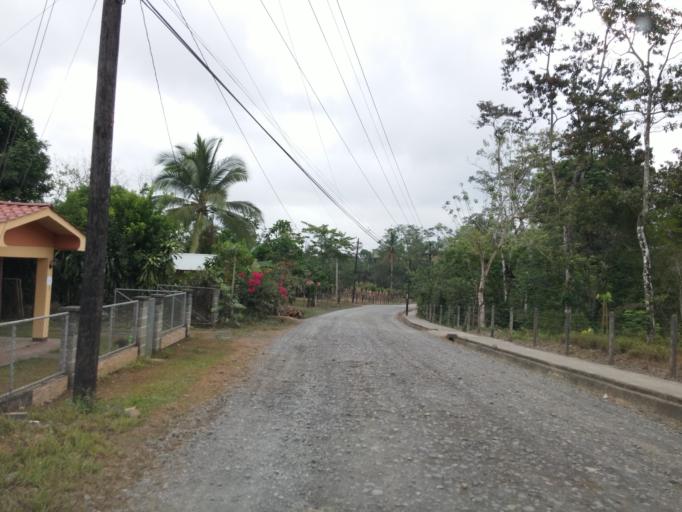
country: CR
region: Alajuela
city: Quesada
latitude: 10.3175
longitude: -84.5202
